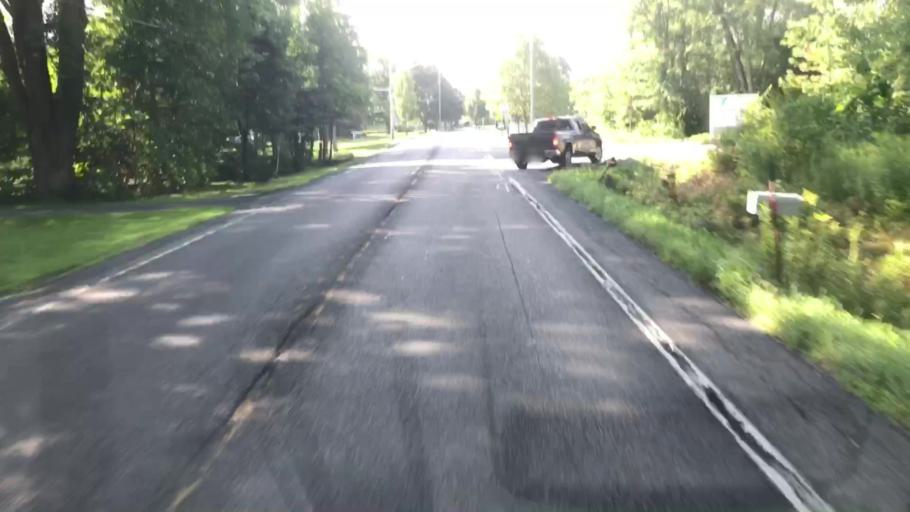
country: US
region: New York
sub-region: Onondaga County
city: Skaneateles
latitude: 42.9551
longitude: -76.4257
